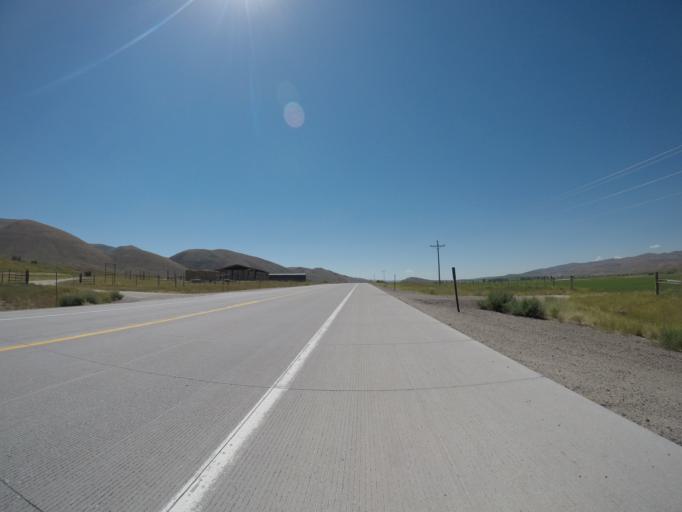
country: US
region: Idaho
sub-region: Bear Lake County
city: Montpelier
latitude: 42.1592
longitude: -110.9852
